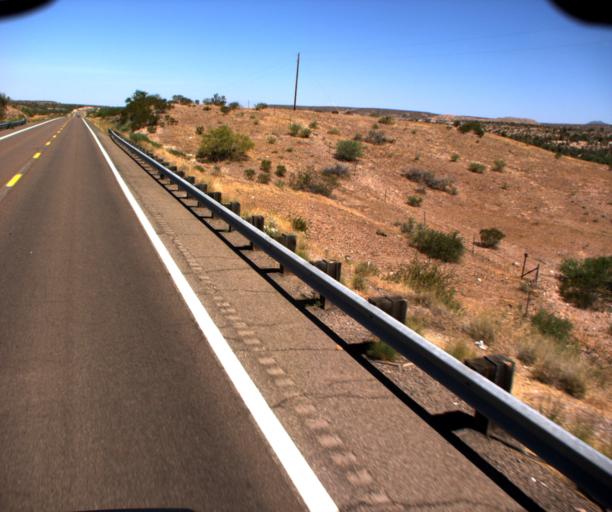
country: US
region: Arizona
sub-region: Graham County
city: Bylas
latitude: 33.2032
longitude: -110.1930
